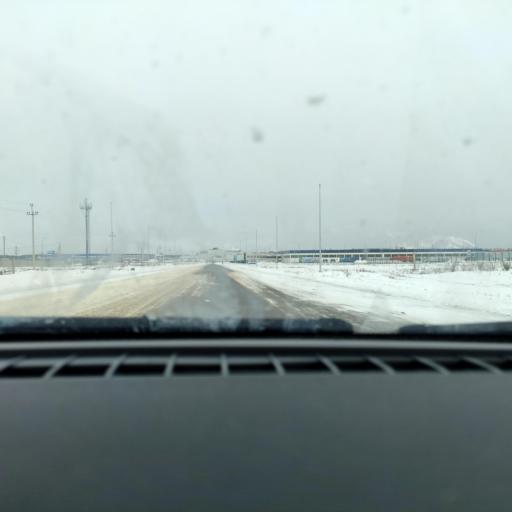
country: RU
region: Voronezj
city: Maslovka
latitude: 51.5414
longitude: 39.2744
